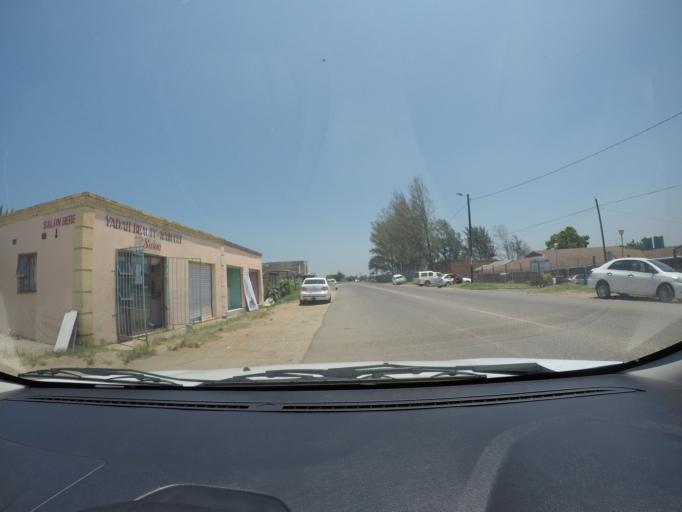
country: ZA
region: KwaZulu-Natal
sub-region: uThungulu District Municipality
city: eSikhawini
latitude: -28.8898
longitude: 31.8938
